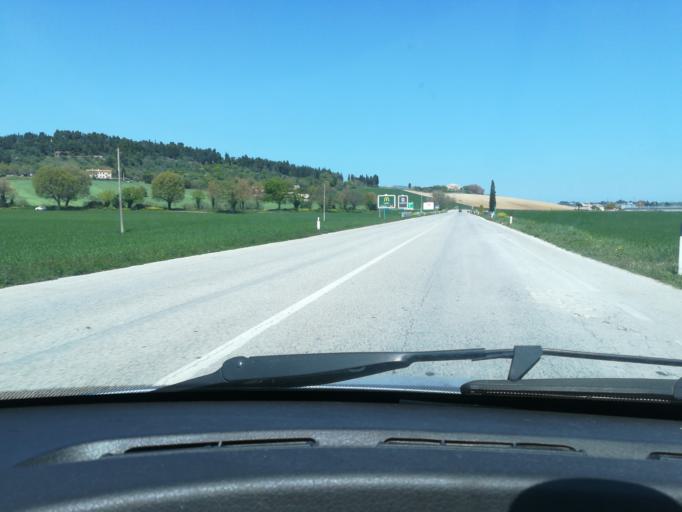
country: IT
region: The Marches
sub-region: Provincia di Ancona
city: Villa Musone
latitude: 43.4586
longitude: 13.5970
